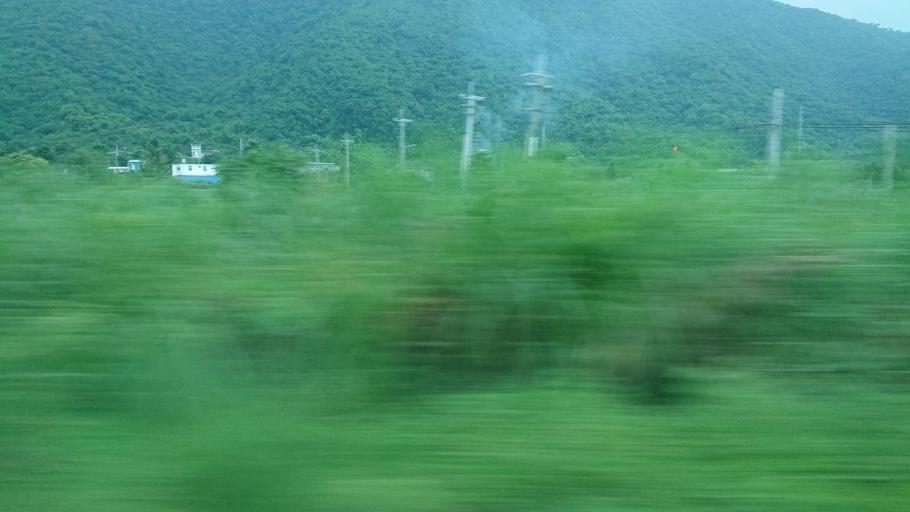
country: TW
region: Taiwan
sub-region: Hualien
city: Hualian
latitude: 24.1160
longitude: 121.6284
